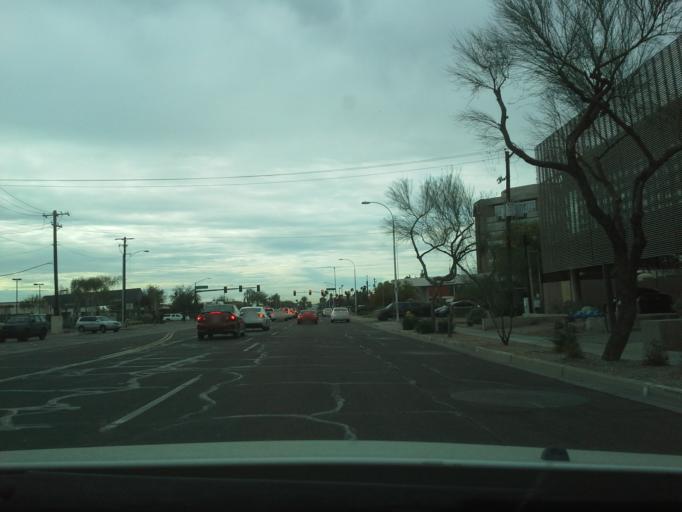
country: US
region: Arizona
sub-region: Maricopa County
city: Paradise Valley
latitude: 33.4818
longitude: -111.9872
